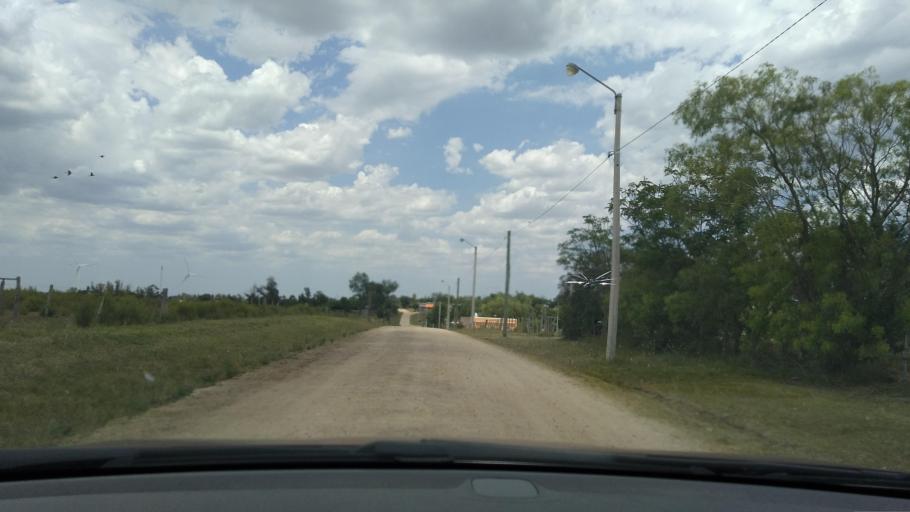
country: UY
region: Canelones
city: Tala
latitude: -34.1960
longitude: -55.7306
